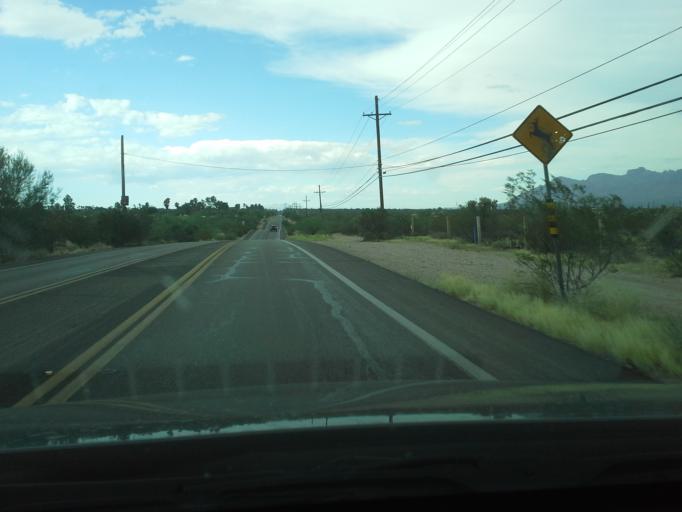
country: US
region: Arizona
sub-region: Pima County
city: South Tucson
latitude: 32.2111
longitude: -111.0203
